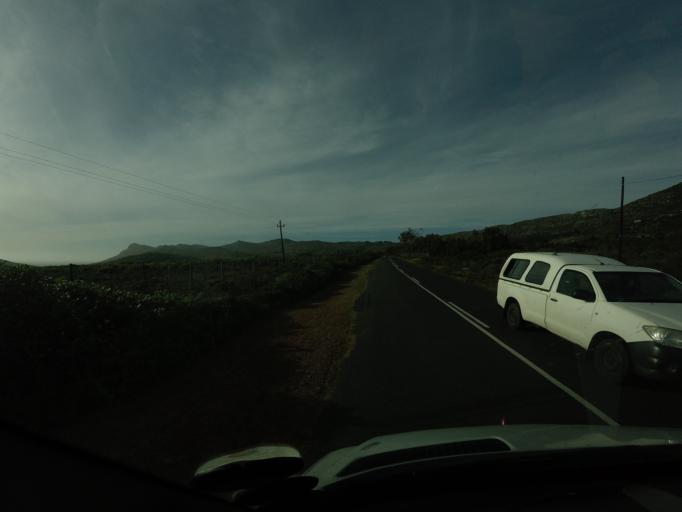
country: ZA
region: Western Cape
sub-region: City of Cape Town
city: Bergvliet
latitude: -34.2182
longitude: 18.4073
